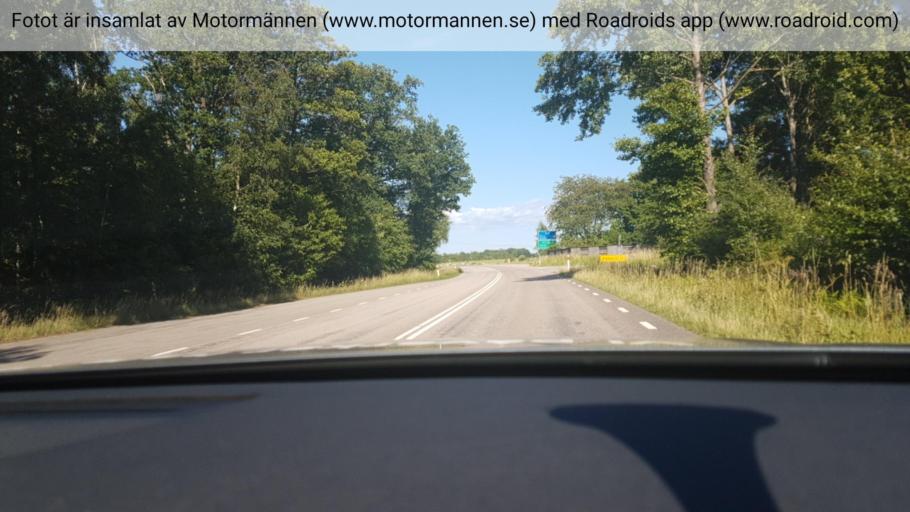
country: SE
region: Halland
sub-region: Falkenbergs Kommun
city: Falkenberg
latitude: 56.8993
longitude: 12.5697
